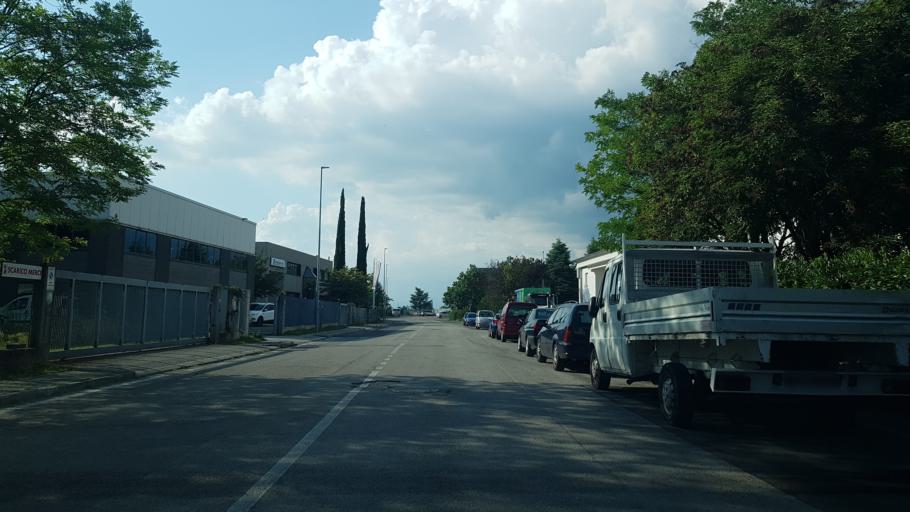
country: IT
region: Friuli Venezia Giulia
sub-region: Provincia di Gorizia
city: Begliano
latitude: 45.8225
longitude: 13.4750
